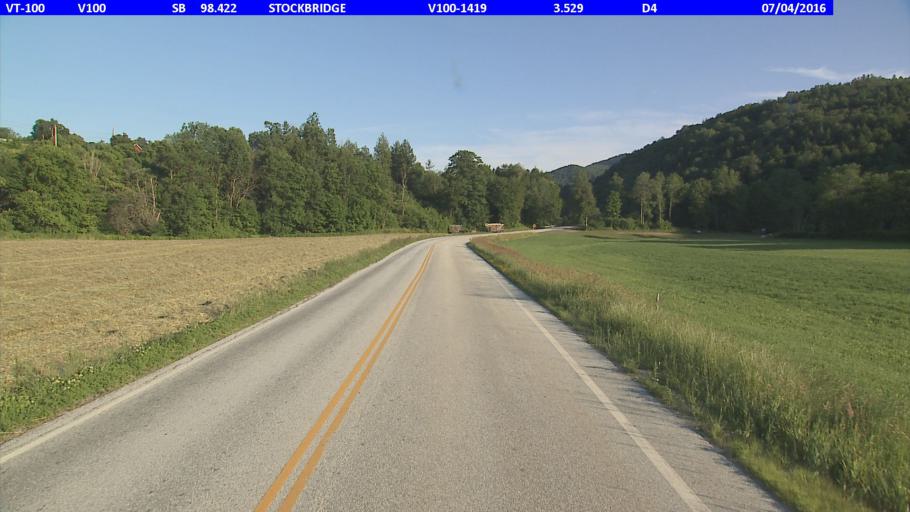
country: US
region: Vermont
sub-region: Orange County
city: Randolph
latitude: 43.7896
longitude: -72.7607
